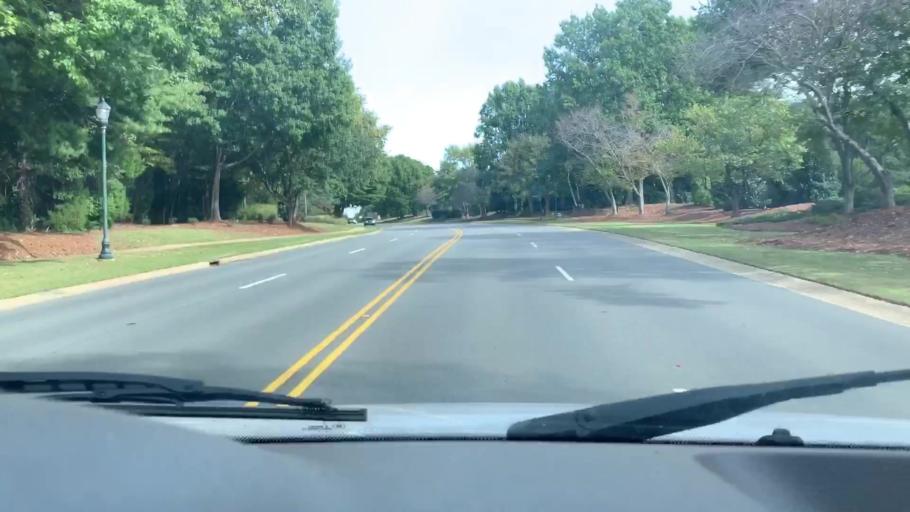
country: US
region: North Carolina
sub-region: Mecklenburg County
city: Cornelius
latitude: 35.4756
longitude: -80.9033
